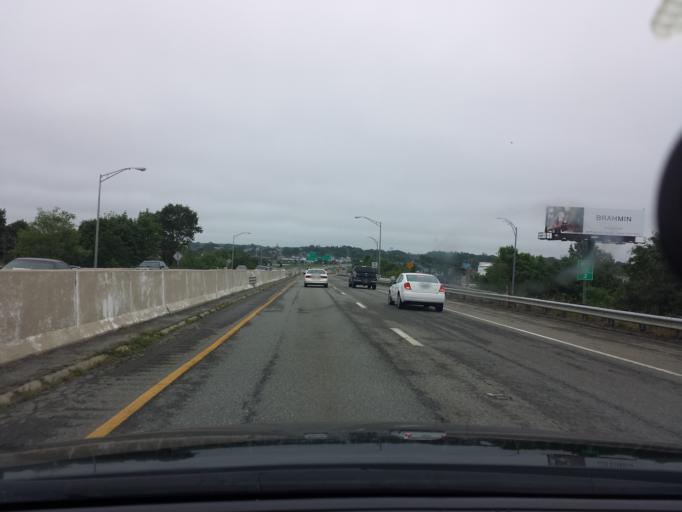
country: US
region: Massachusetts
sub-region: Bristol County
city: New Bedford
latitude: 41.6543
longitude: -70.9266
